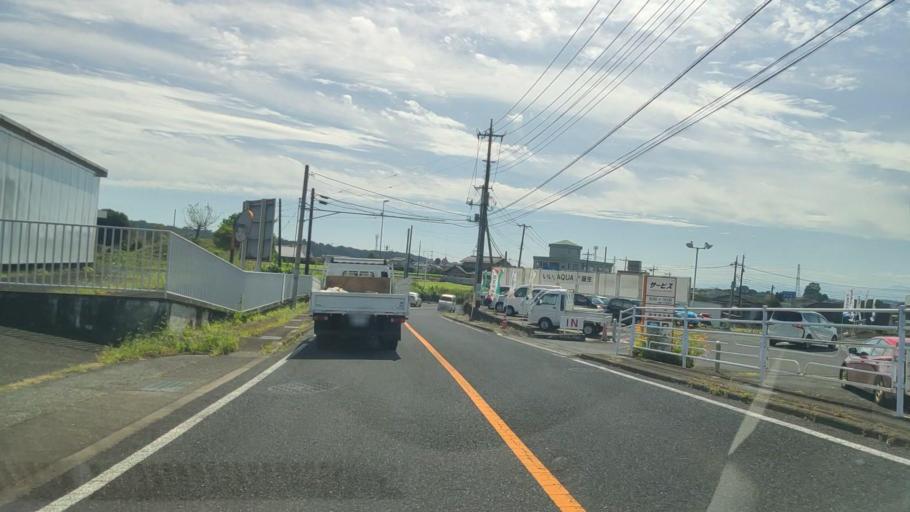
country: JP
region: Gunma
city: Shibukawa
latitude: 36.5242
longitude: 139.0110
